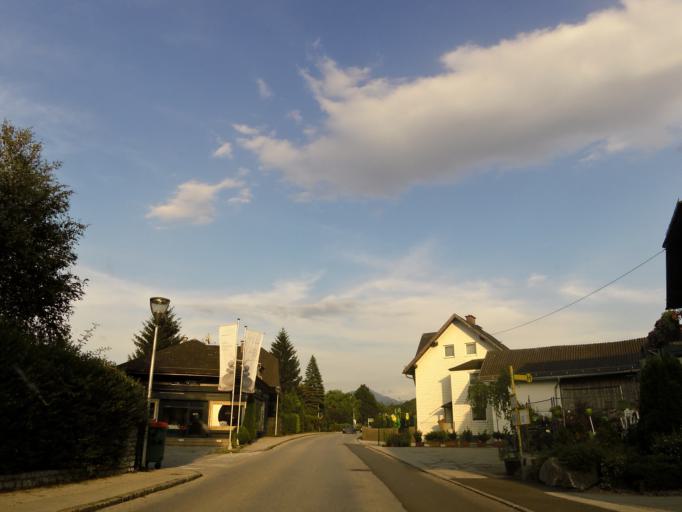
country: AT
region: Salzburg
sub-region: Politischer Bezirk Salzburg-Umgebung
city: Grodig
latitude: 47.7378
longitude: 13.0407
